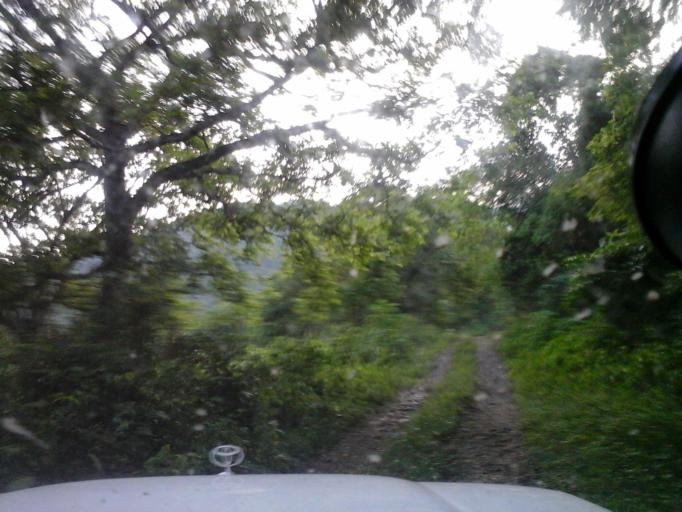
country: CO
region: Cesar
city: Agustin Codazzi
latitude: 10.1734
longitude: -73.1459
